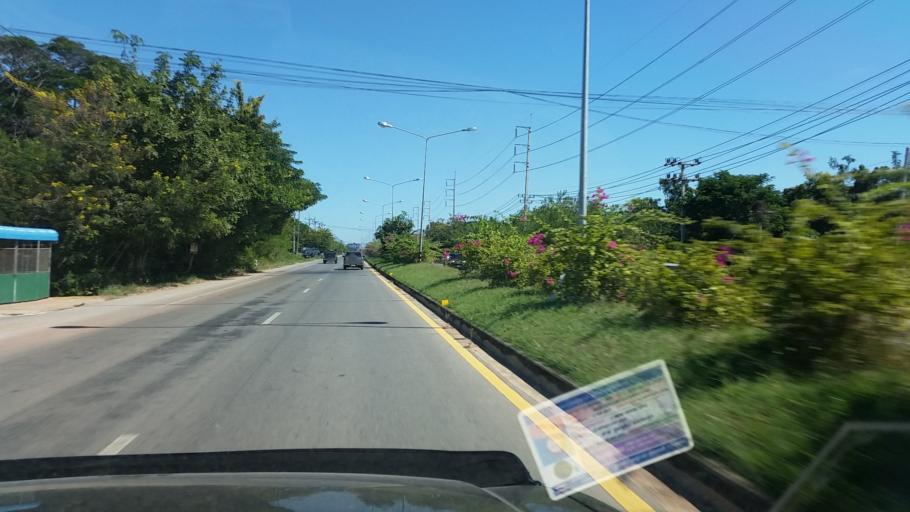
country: TH
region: Chaiyaphum
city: Chaiyaphum
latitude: 15.7918
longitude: 101.9970
